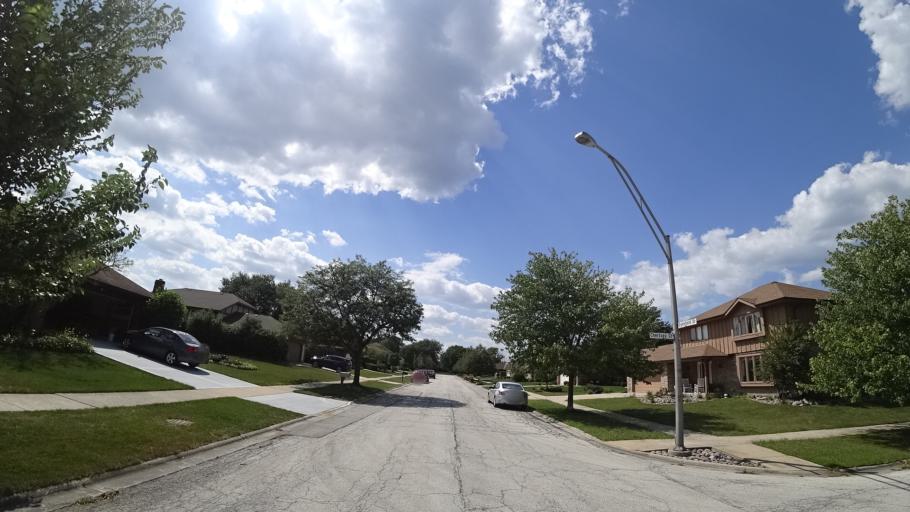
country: US
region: Illinois
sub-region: Cook County
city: Orland Park
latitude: 41.6287
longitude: -87.8207
